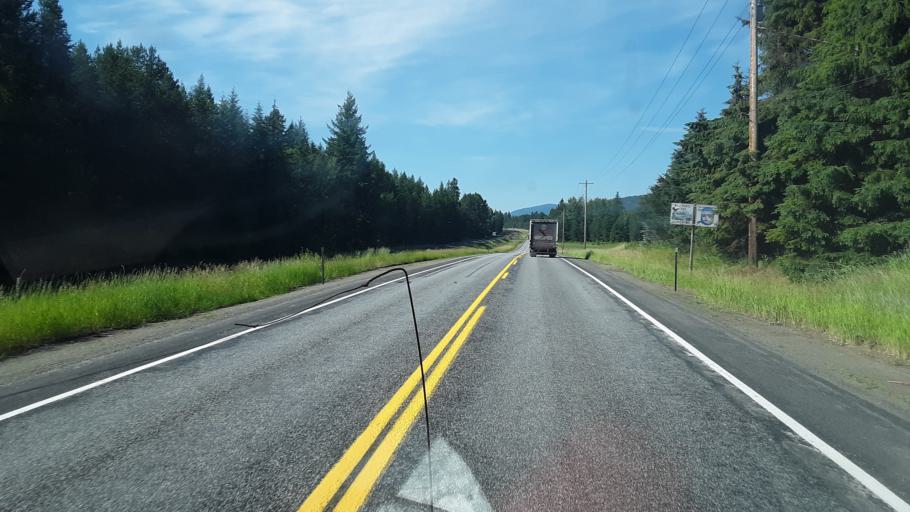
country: US
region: Idaho
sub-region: Bonner County
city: Ponderay
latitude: 48.4972
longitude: -116.4517
